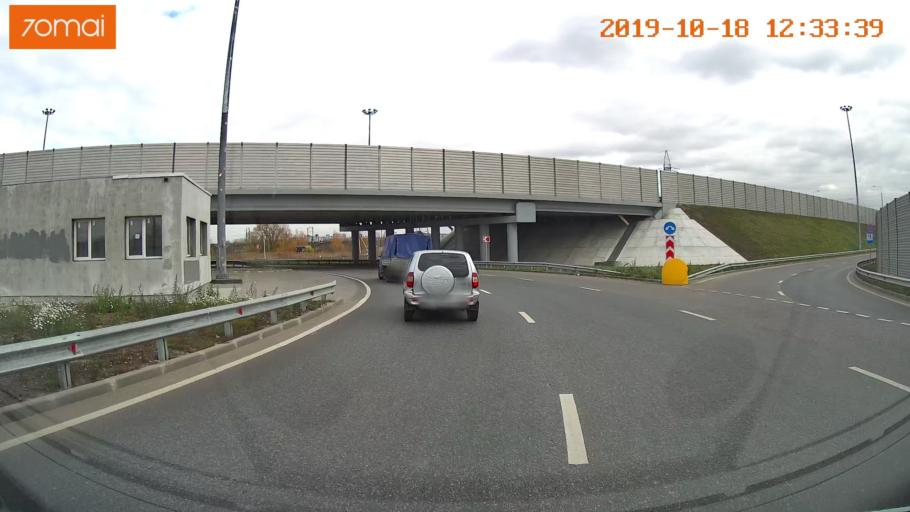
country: RU
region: Rjazan
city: Ryazan'
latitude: 54.6093
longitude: 39.6396
